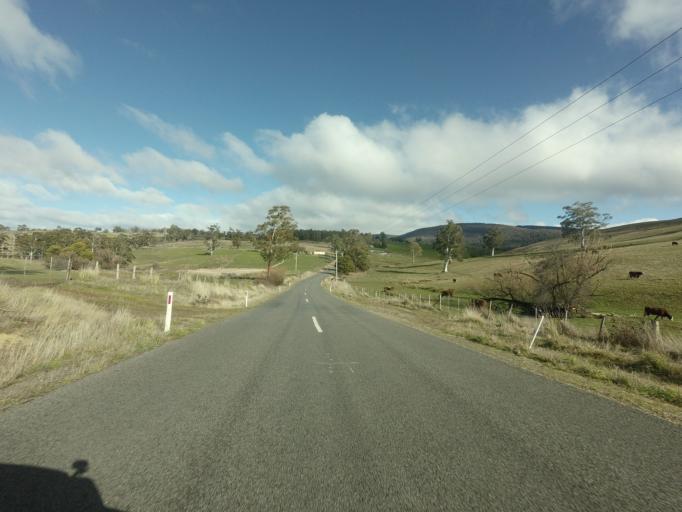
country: AU
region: Tasmania
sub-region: Derwent Valley
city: New Norfolk
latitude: -42.5645
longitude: 146.7042
